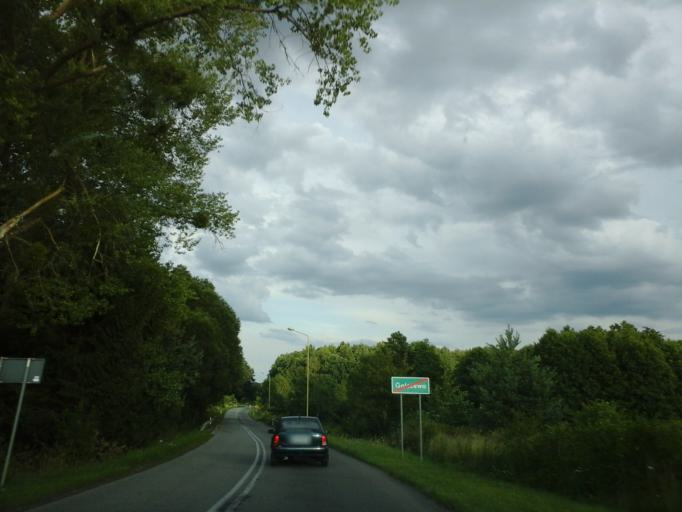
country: PL
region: West Pomeranian Voivodeship
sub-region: Powiat kamienski
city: Golczewo
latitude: 53.8184
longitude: 14.9913
